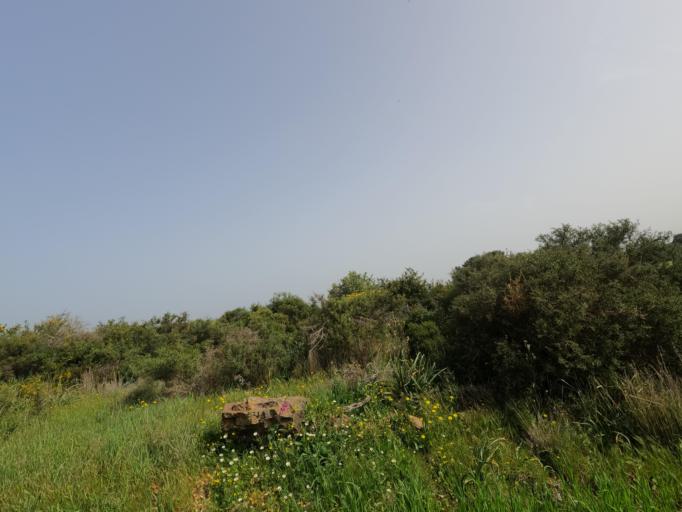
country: CY
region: Pafos
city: Polis
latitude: 35.0080
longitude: 32.3592
